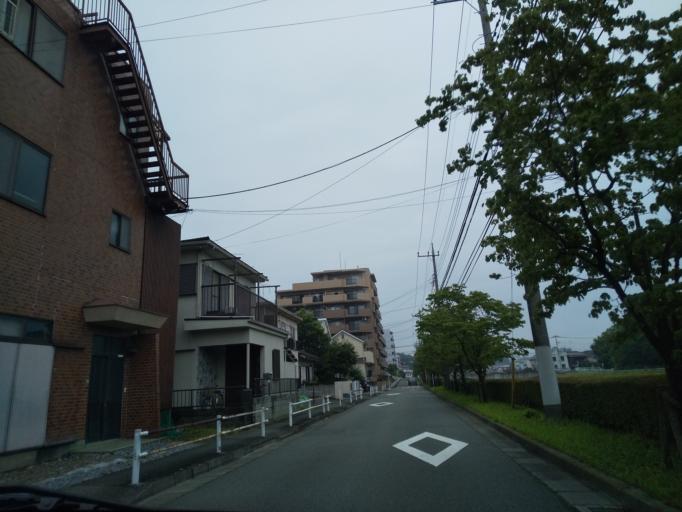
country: JP
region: Tokyo
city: Hino
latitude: 35.6453
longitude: 139.4318
